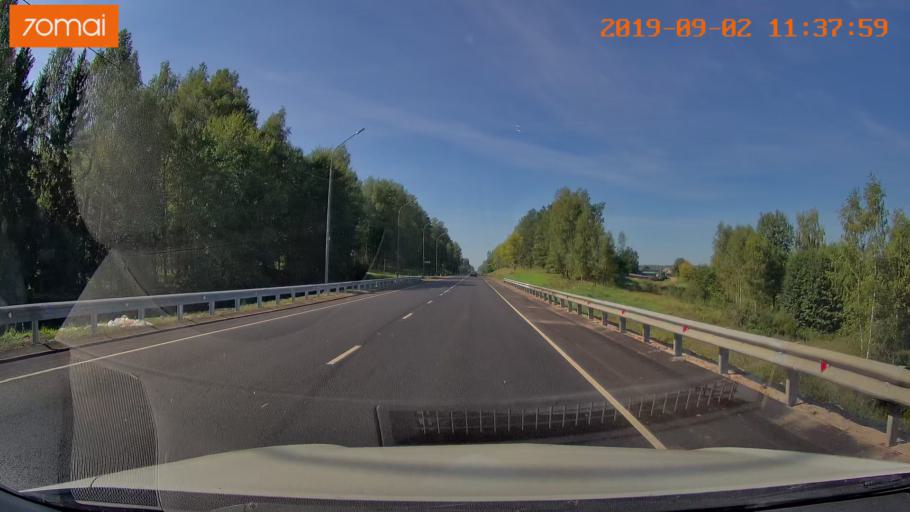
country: RU
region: Smolensk
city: Oster
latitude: 53.9157
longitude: 32.7486
